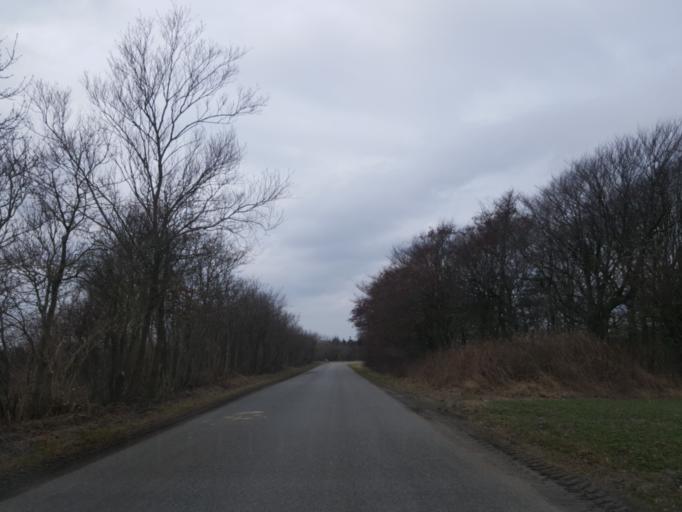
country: DK
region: Central Jutland
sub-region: Holstebro Kommune
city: Ulfborg
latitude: 56.3664
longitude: 8.2391
